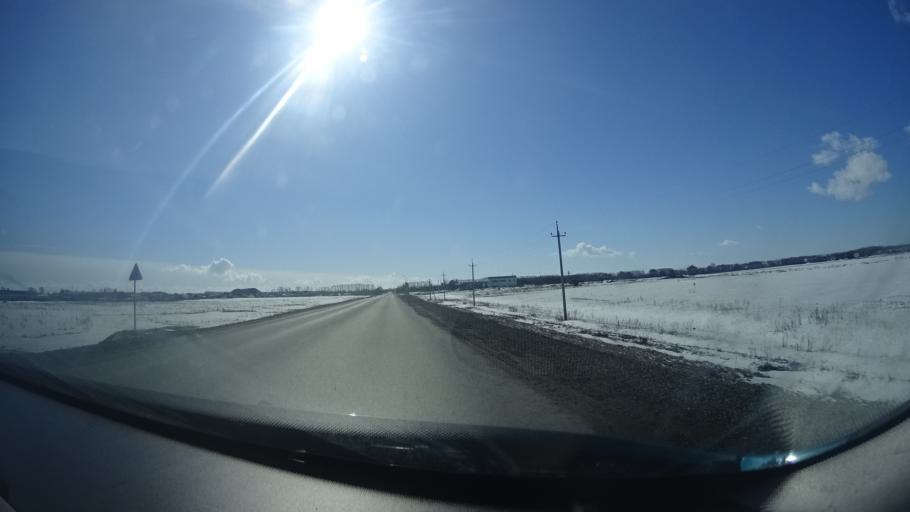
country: RU
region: Bashkortostan
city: Ufa
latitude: 54.6231
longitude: 55.8932
